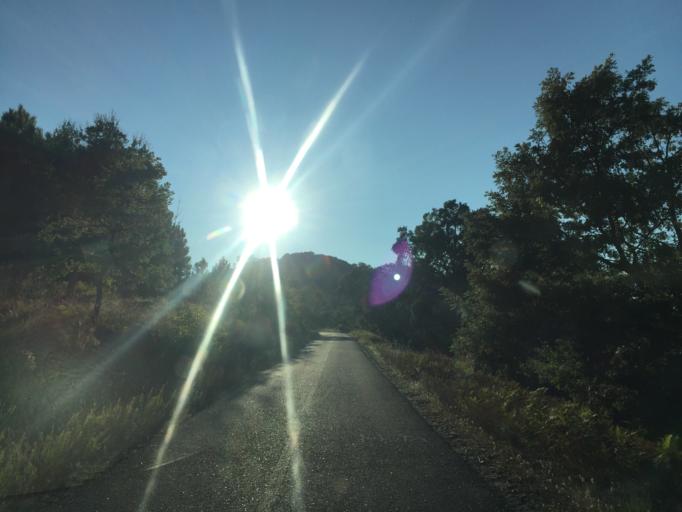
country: PT
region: Portalegre
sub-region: Castelo de Vide
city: Castelo de Vide
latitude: 39.4037
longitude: -7.4468
